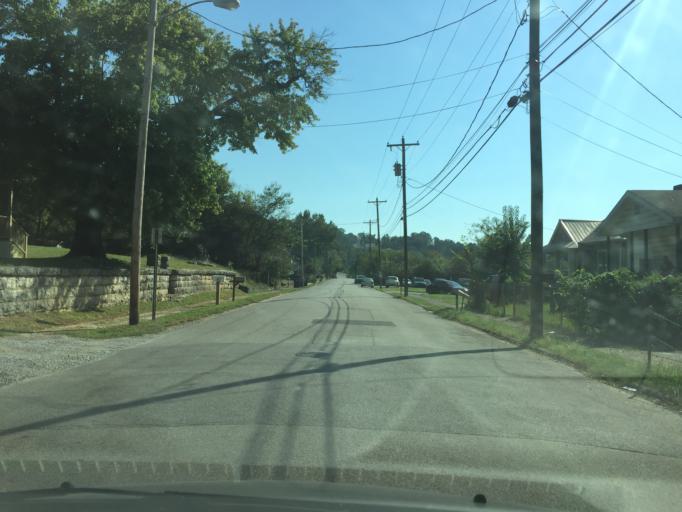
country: US
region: Tennessee
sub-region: Hamilton County
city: Chattanooga
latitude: 35.0687
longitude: -85.3152
